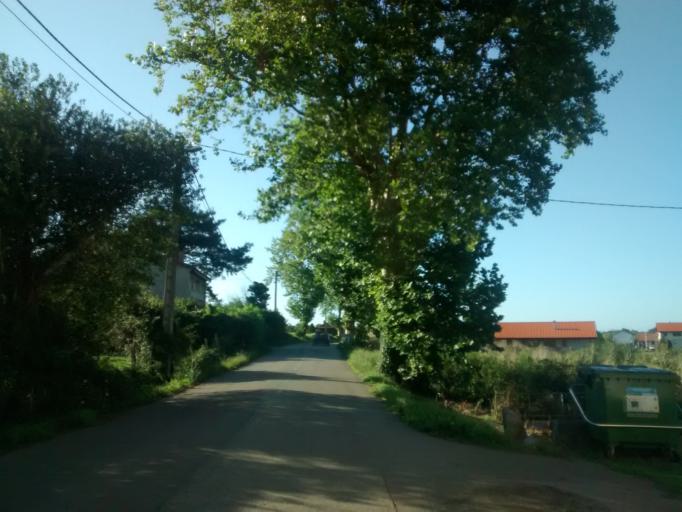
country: ES
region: Cantabria
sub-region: Provincia de Cantabria
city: Santander
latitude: 43.4186
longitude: -3.7489
